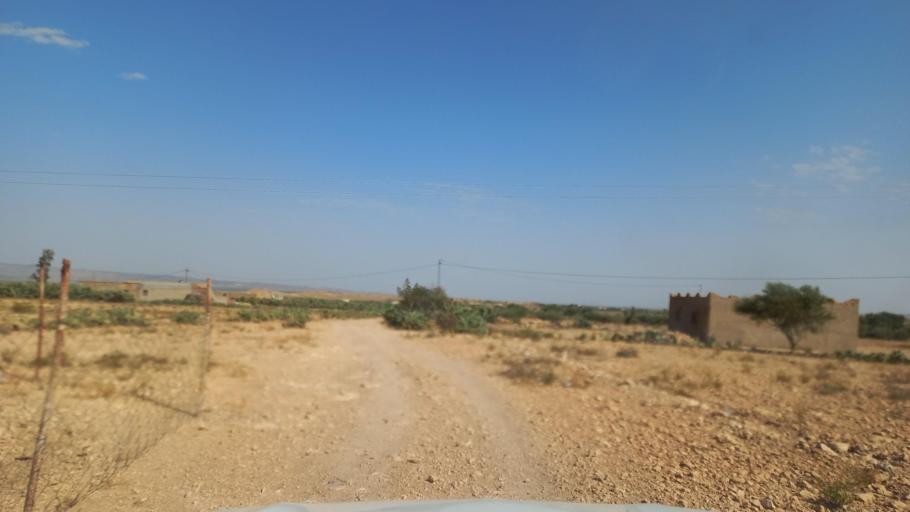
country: TN
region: Al Qasrayn
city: Kasserine
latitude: 35.2832
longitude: 8.9465
